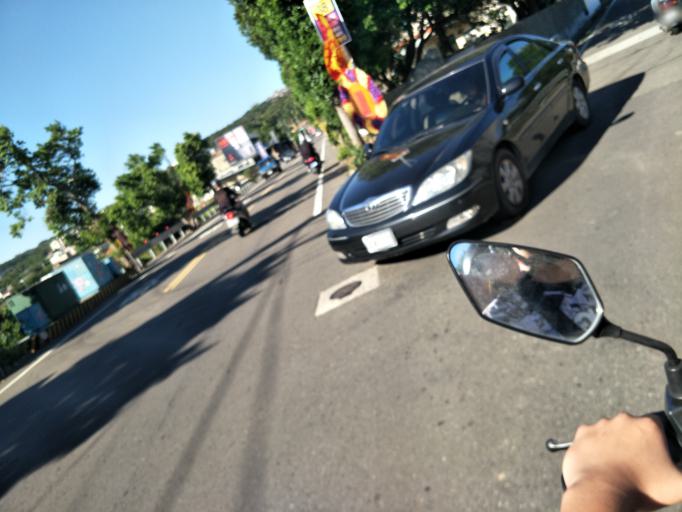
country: TW
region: Taiwan
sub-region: Hsinchu
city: Zhubei
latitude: 24.8408
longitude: 121.0366
